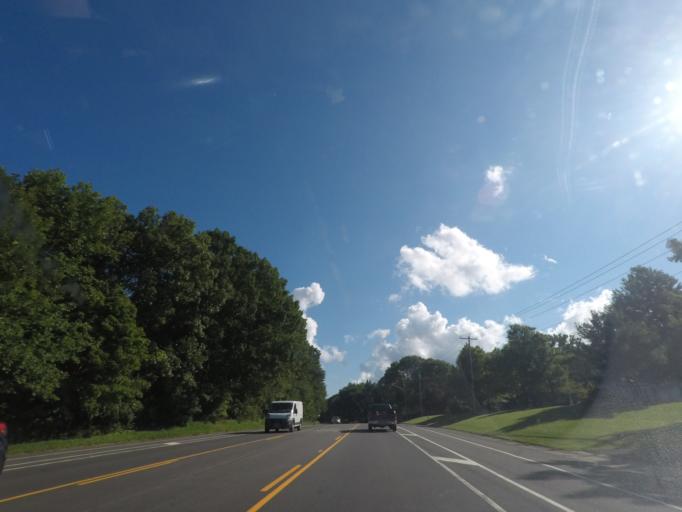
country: US
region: New York
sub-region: Albany County
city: Menands
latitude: 42.6956
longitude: -73.7400
